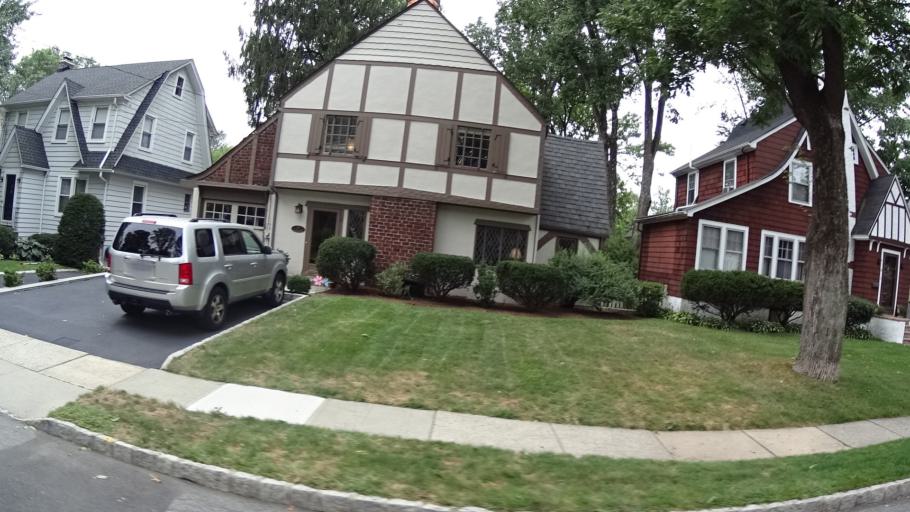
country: US
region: New Jersey
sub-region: Union County
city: New Providence
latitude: 40.7113
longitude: -74.3851
